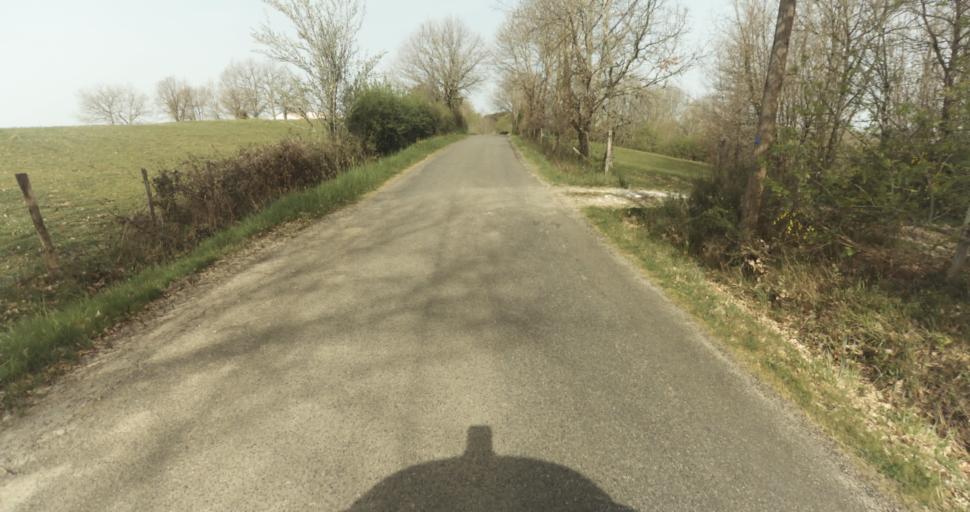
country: FR
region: Midi-Pyrenees
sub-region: Departement du Tarn-et-Garonne
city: Moissac
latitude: 44.1400
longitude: 1.0919
